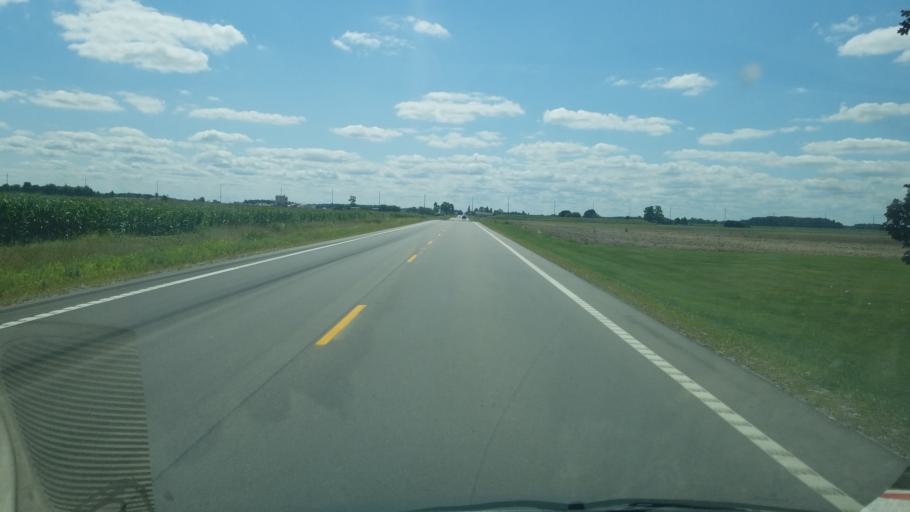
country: US
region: Ohio
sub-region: Fulton County
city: Delta
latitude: 41.7085
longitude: -84.0371
